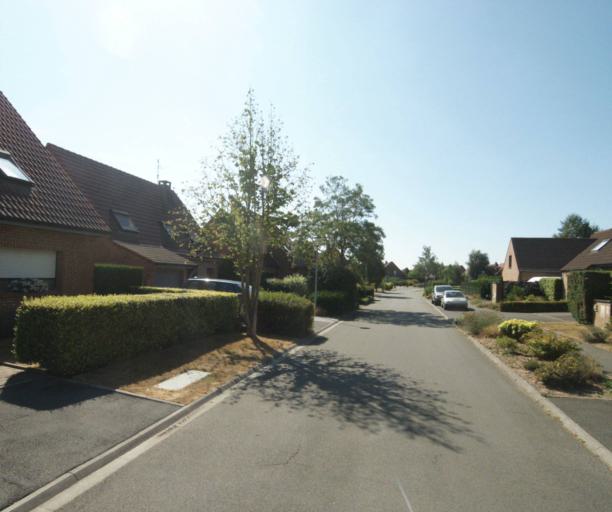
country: FR
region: Nord-Pas-de-Calais
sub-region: Departement du Nord
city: Halluin
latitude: 50.7746
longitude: 3.1151
